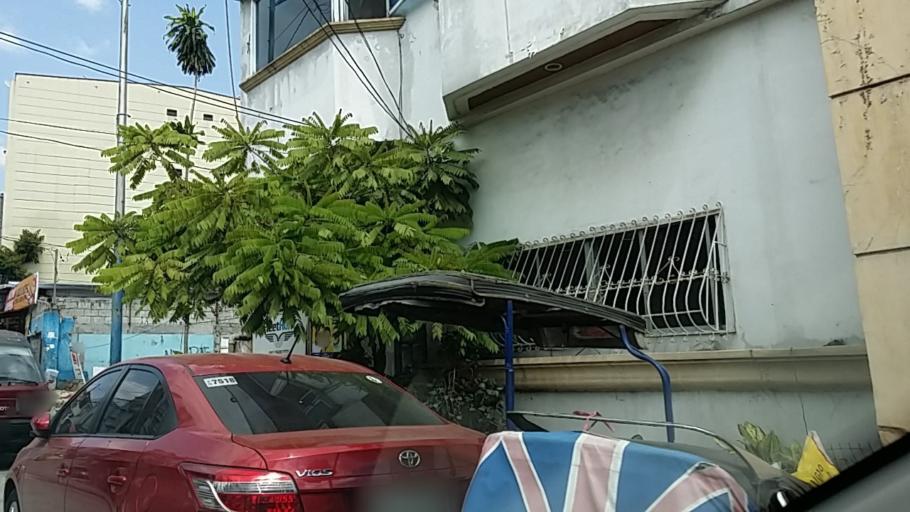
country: PH
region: Metro Manila
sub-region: Mandaluyong
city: Mandaluyong City
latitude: 14.5804
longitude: 121.0485
